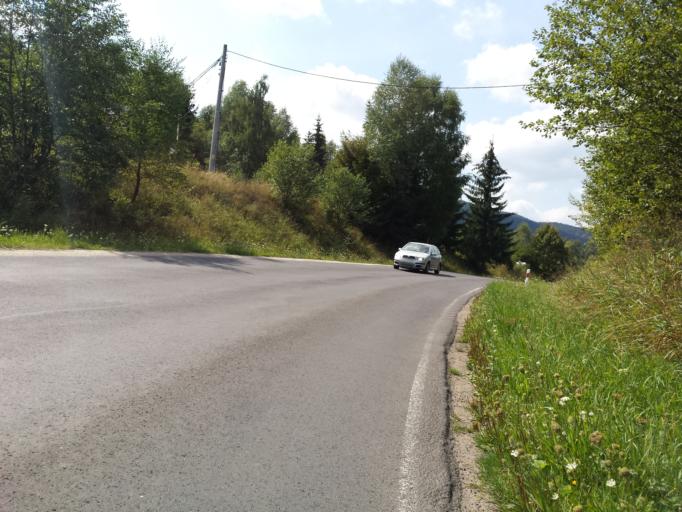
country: PL
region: Subcarpathian Voivodeship
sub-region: Powiat leski
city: Cisna
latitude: 49.1846
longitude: 22.3868
